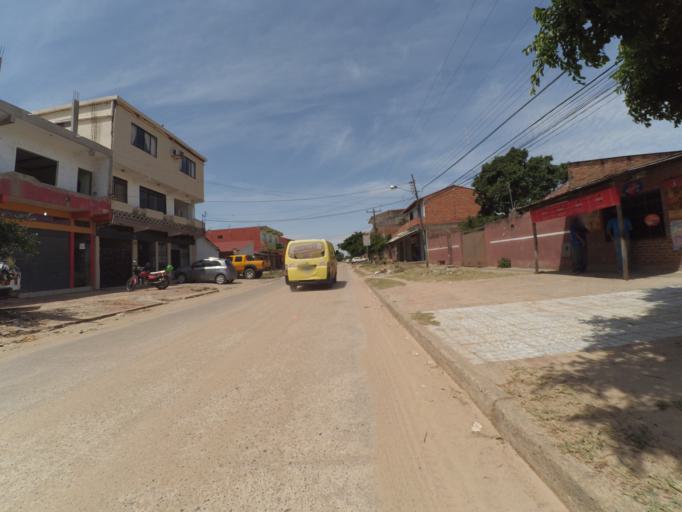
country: BO
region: Santa Cruz
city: Santa Cruz de la Sierra
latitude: -17.8261
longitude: -63.2294
